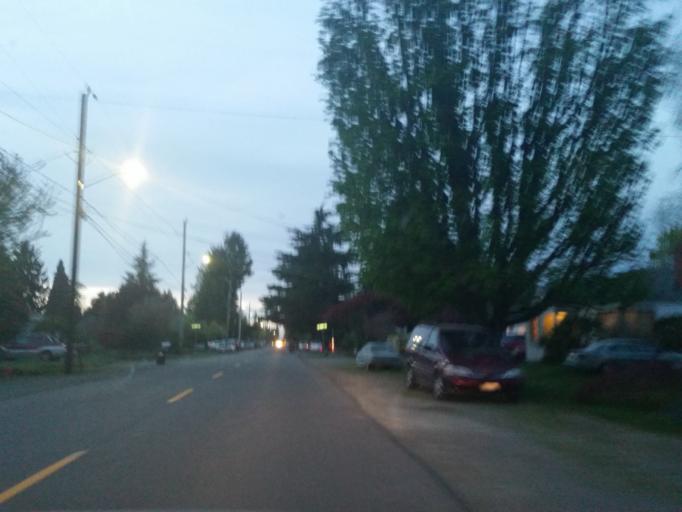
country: US
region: Washington
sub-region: King County
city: Shoreline
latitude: 47.7098
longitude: -122.3529
